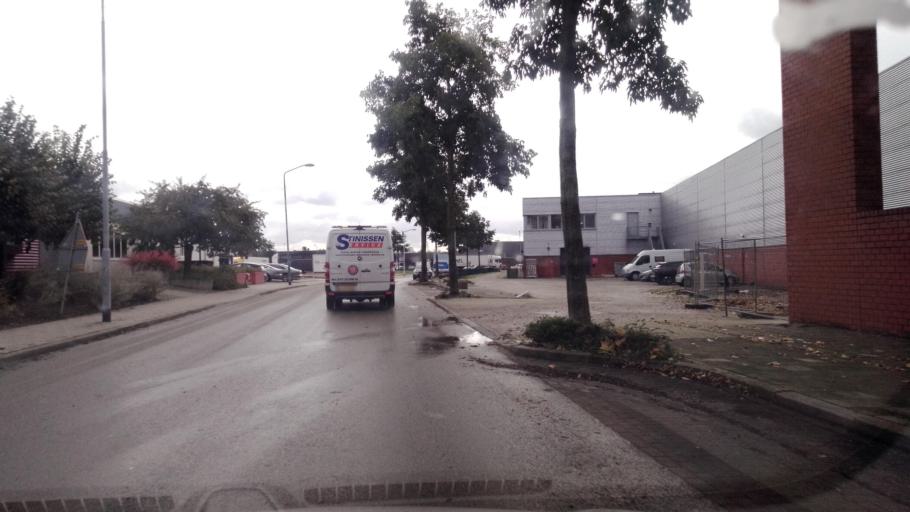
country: NL
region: Limburg
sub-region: Gemeente Venlo
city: Venlo
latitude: 51.3867
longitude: 6.1792
